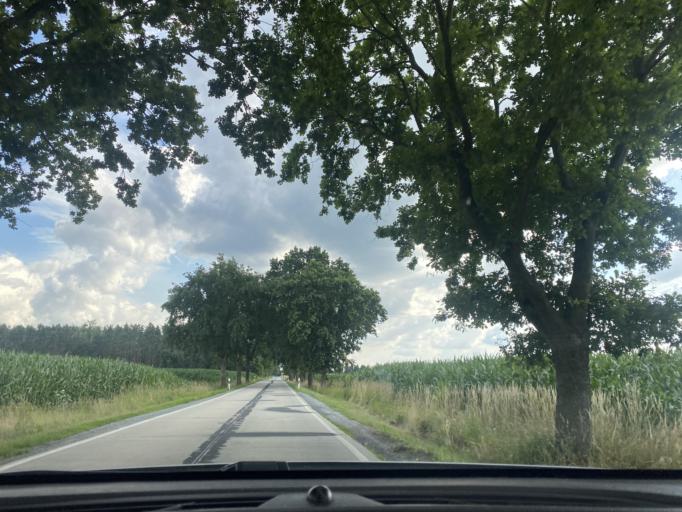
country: DE
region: Saxony
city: Klitten
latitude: 51.3586
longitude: 14.6077
